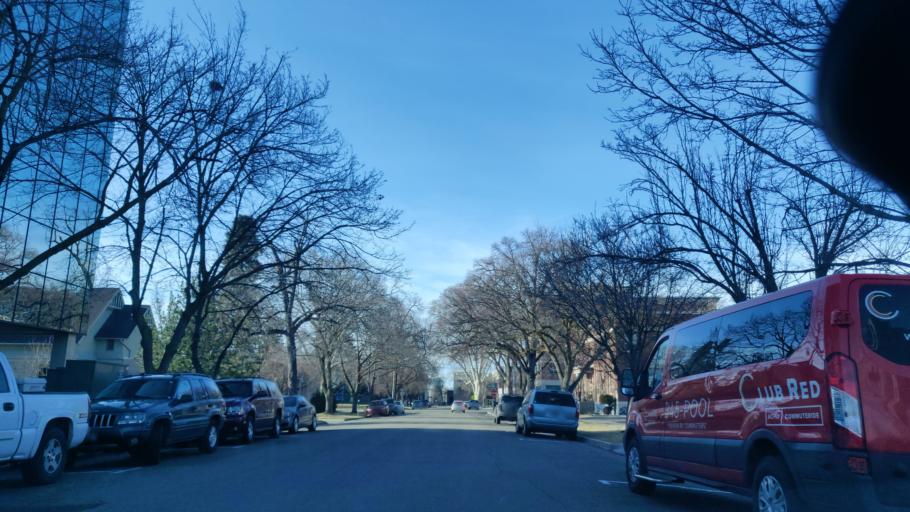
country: US
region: Idaho
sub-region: Ada County
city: Boise
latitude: 43.6190
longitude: -116.1988
